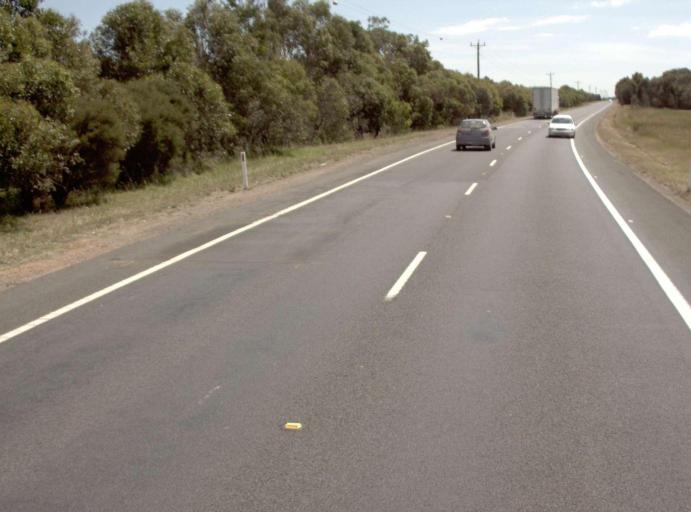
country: AU
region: Victoria
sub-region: Wellington
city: Sale
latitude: -38.0997
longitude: 146.9709
